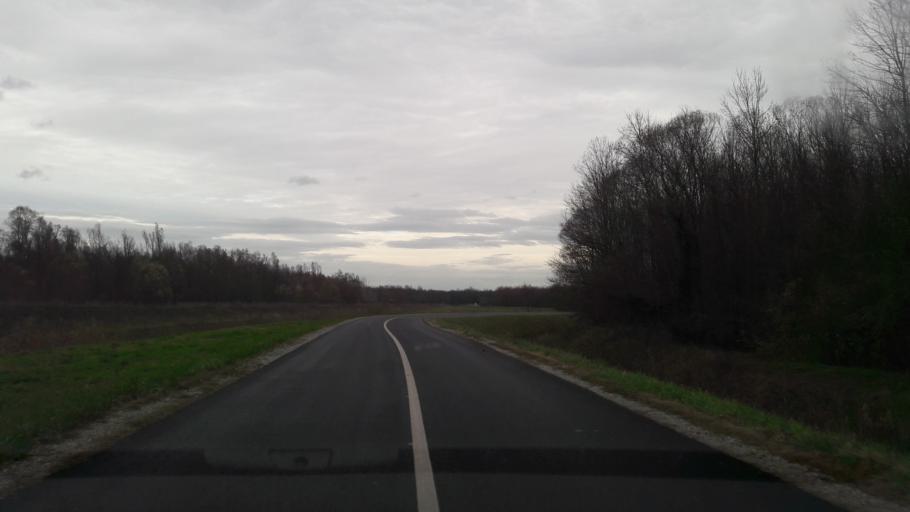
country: HR
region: Osjecko-Baranjska
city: Velimirovac
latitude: 45.6221
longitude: 18.0813
